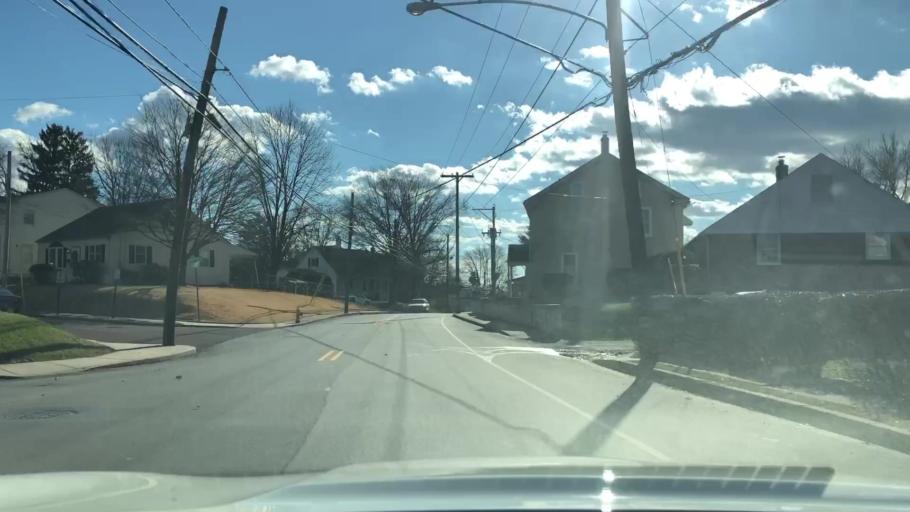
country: US
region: Pennsylvania
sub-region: Montgomery County
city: Pottstown
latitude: 40.2553
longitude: -75.6553
